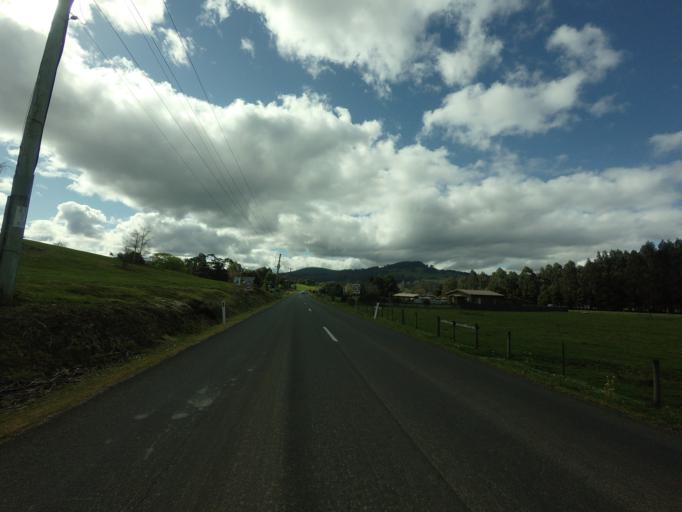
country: AU
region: Tasmania
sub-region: Huon Valley
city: Geeveston
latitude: -43.1734
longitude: 146.9239
